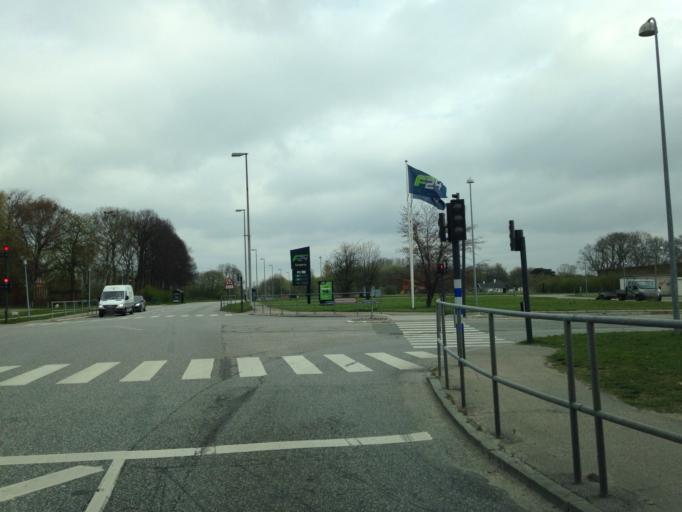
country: DK
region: Capital Region
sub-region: Ishoj Kommune
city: Ishoj
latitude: 55.6048
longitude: 12.3259
